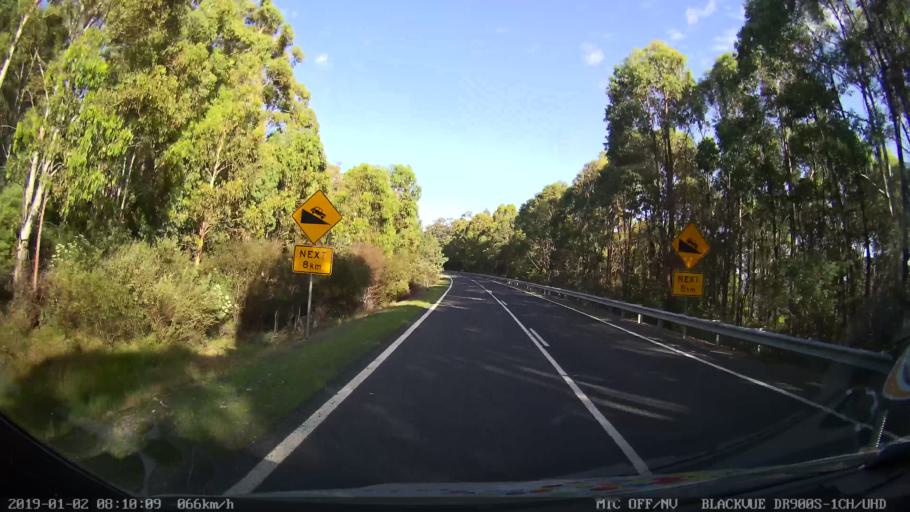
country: AU
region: New South Wales
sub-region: Tumut Shire
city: Tumut
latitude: -35.6010
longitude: 148.3733
